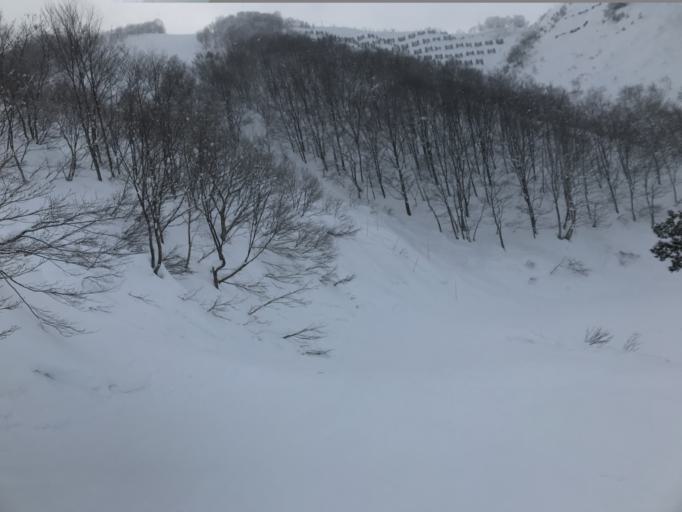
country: JP
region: Nagano
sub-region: Kitaazumi Gun
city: Hakuba
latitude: 36.6989
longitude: 137.8156
